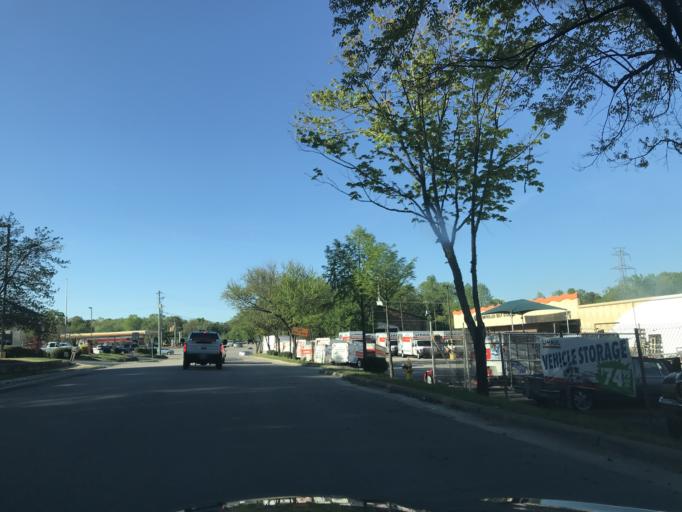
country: US
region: North Carolina
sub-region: Wake County
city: Knightdale
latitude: 35.7965
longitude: -78.5566
